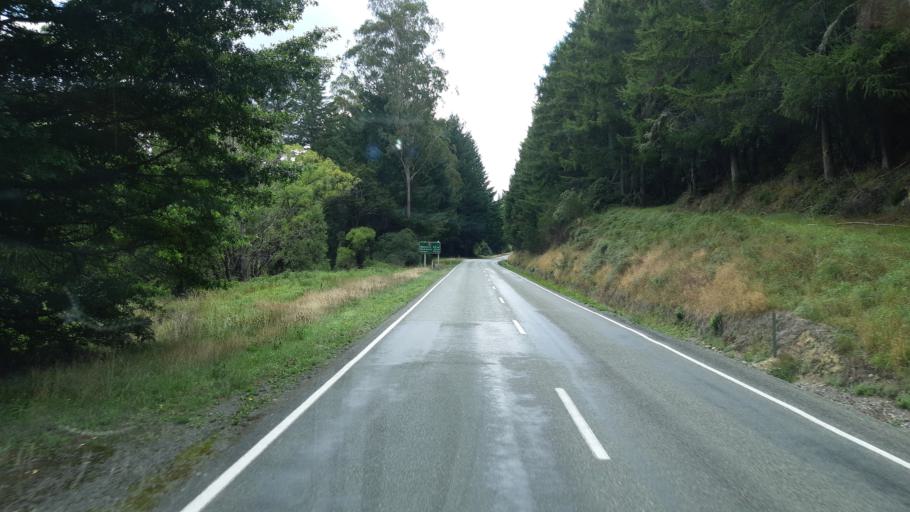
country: NZ
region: Tasman
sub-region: Tasman District
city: Wakefield
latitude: -41.6018
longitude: 172.7588
